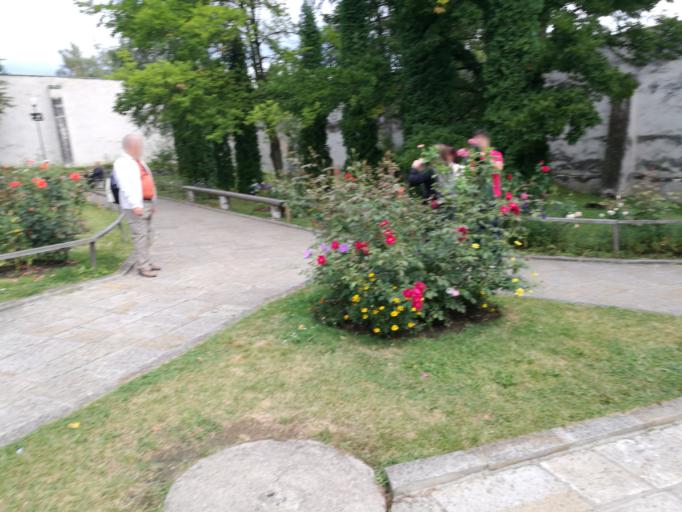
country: RO
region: Suceava
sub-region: Oras Gura Humorului
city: Gura Humorului
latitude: 47.5171
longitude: 25.8645
